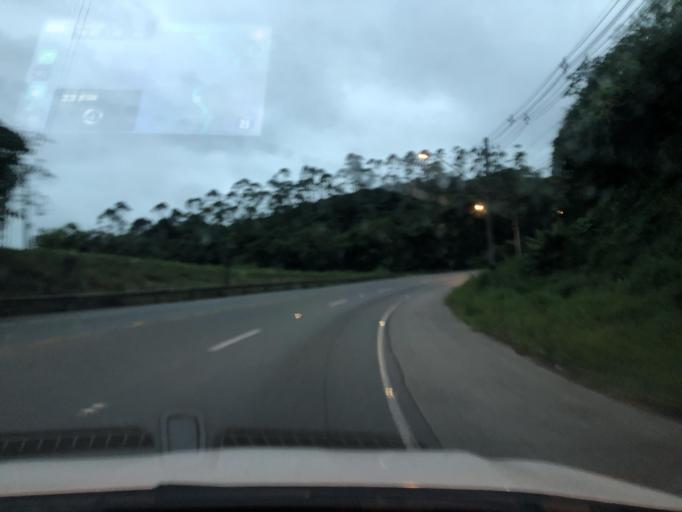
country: BR
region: Santa Catarina
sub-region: Pomerode
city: Pomerode
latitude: -26.7341
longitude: -49.0670
